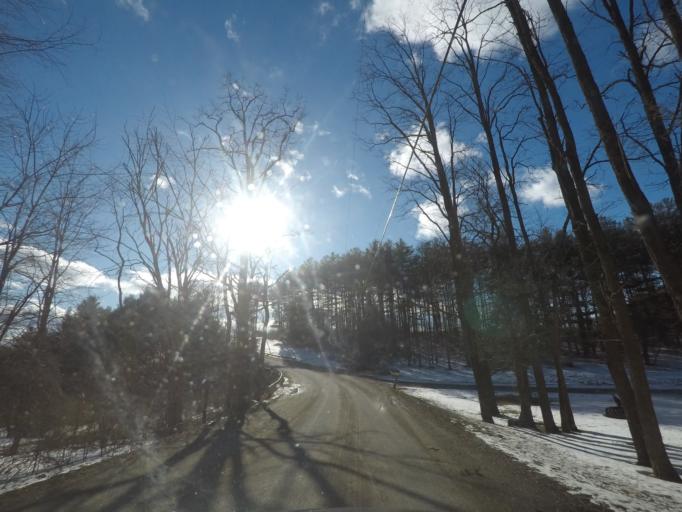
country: US
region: New York
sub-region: Rensselaer County
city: Hoosick Falls
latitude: 42.8387
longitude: -73.4716
